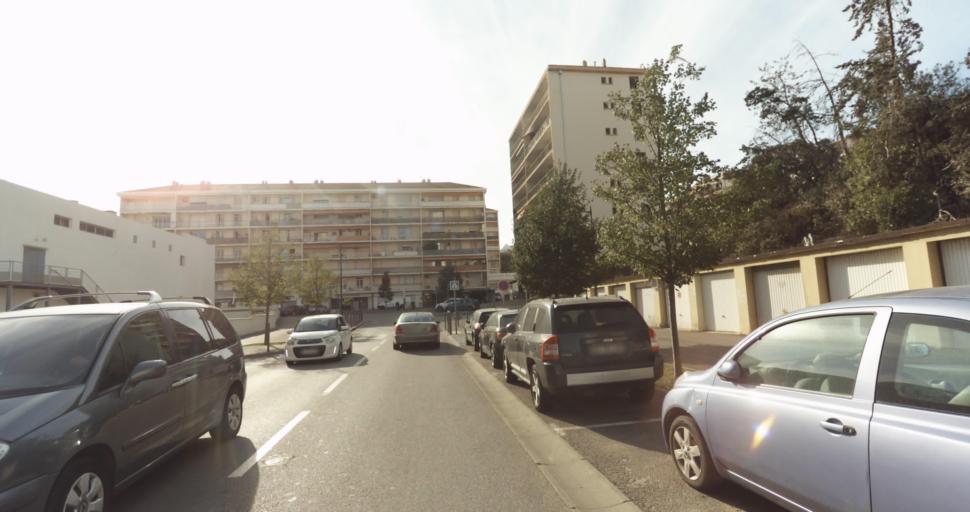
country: FR
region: Corsica
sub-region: Departement de la Corse-du-Sud
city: Ajaccio
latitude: 41.9352
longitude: 8.7463
